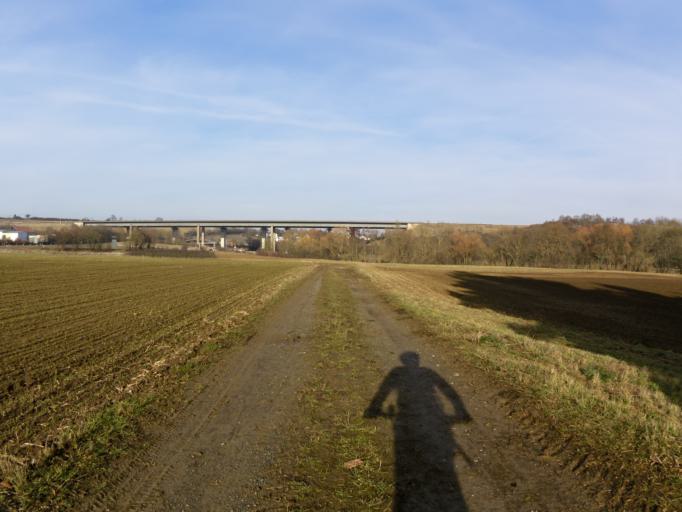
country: DE
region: Bavaria
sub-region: Regierungsbezirk Unterfranken
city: Estenfeld
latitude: 49.8380
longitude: 10.0196
